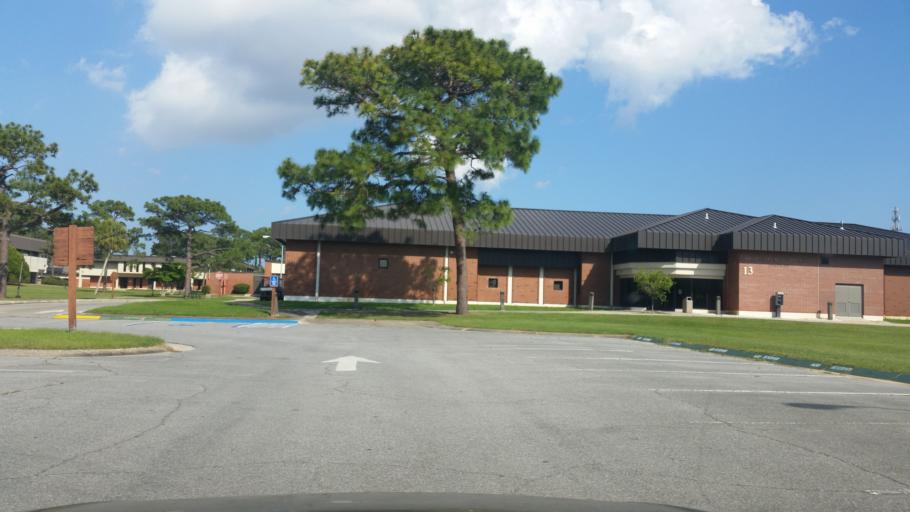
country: US
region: Florida
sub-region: Escambia County
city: Ferry Pass
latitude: 30.4791
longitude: -87.2045
